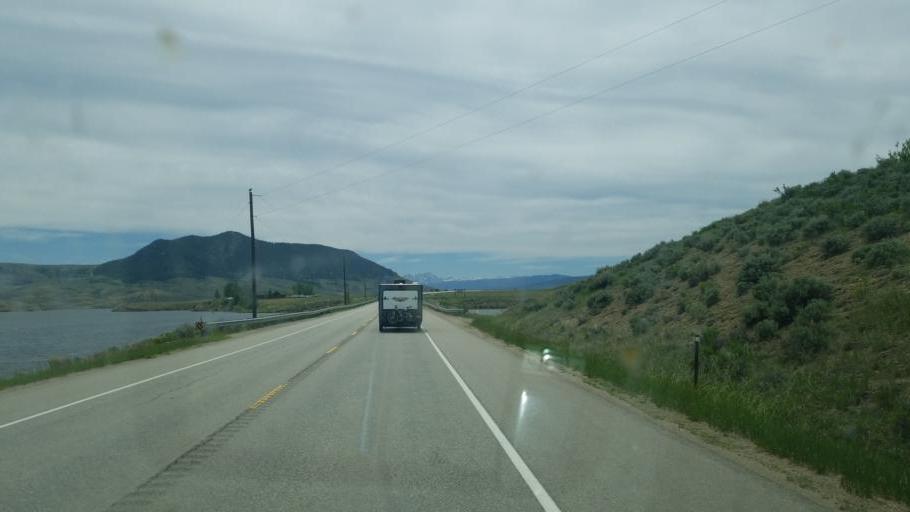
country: US
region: Colorado
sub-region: Grand County
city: Kremmling
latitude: 40.1630
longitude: -106.4167
